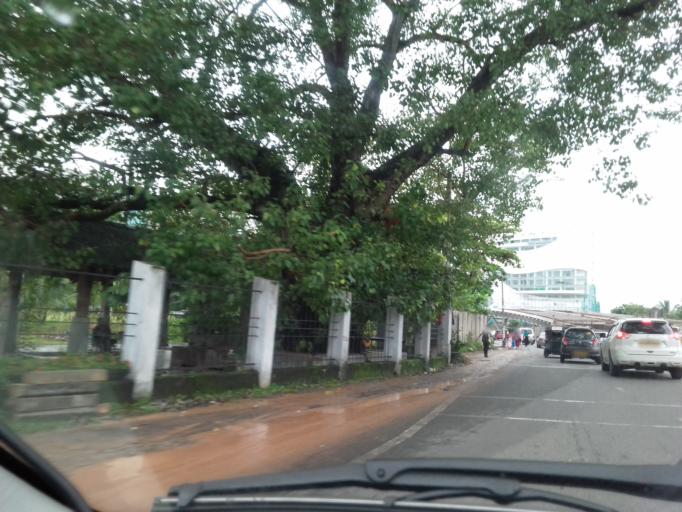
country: LK
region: Western
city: Pita Kotte
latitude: 6.9083
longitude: 79.8937
